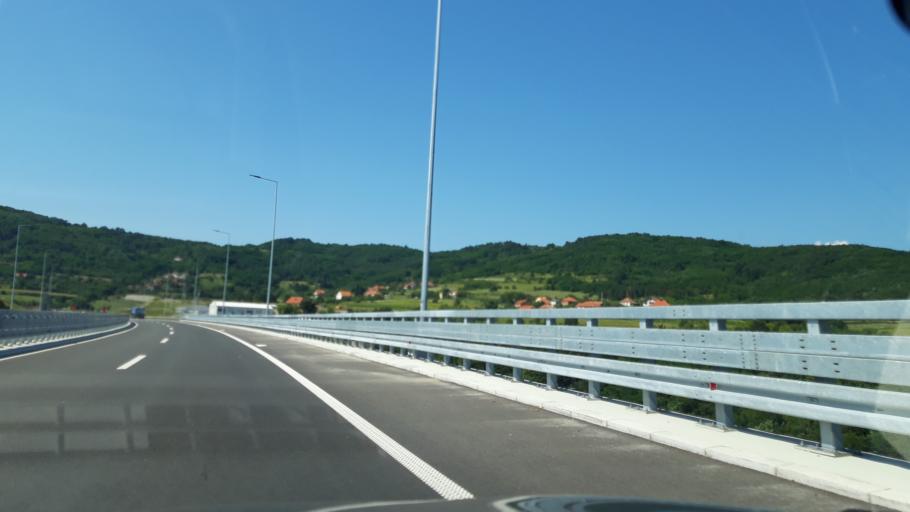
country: RS
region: Central Serbia
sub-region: Pcinjski Okrug
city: Vladicin Han
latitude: 42.7227
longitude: 22.0764
